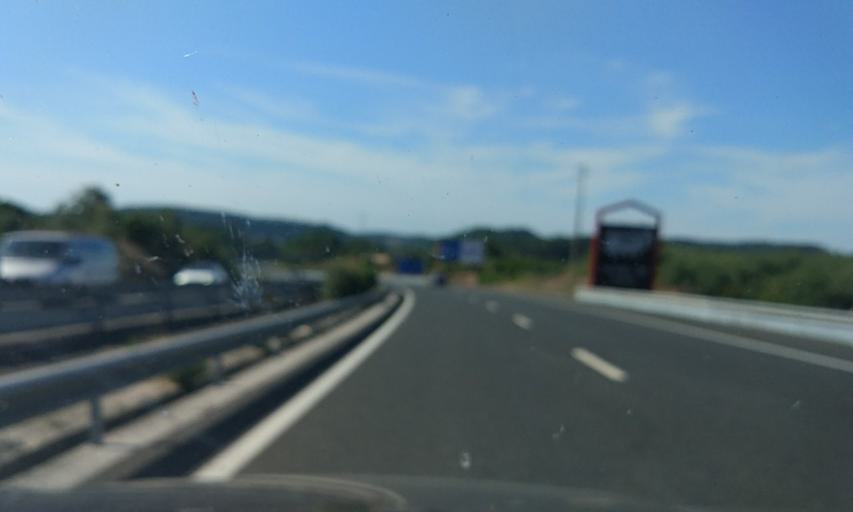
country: PT
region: Leiria
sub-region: Leiria
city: Santa Catarina da Serra
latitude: 39.6992
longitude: -8.7022
